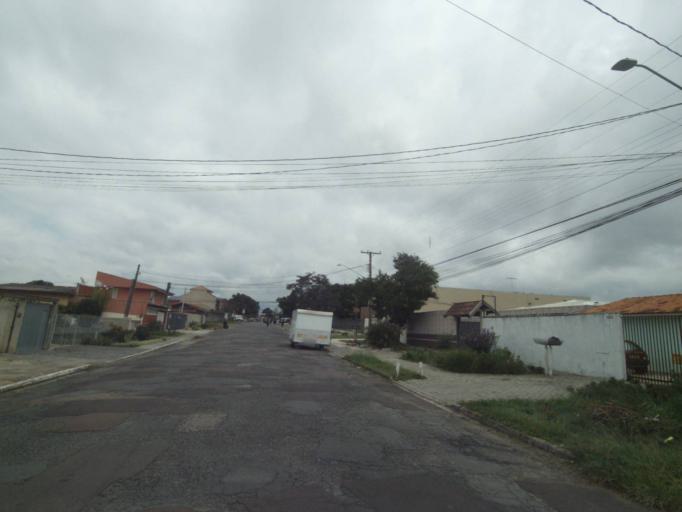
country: BR
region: Parana
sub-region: Pinhais
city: Pinhais
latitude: -25.4600
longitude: -49.2099
